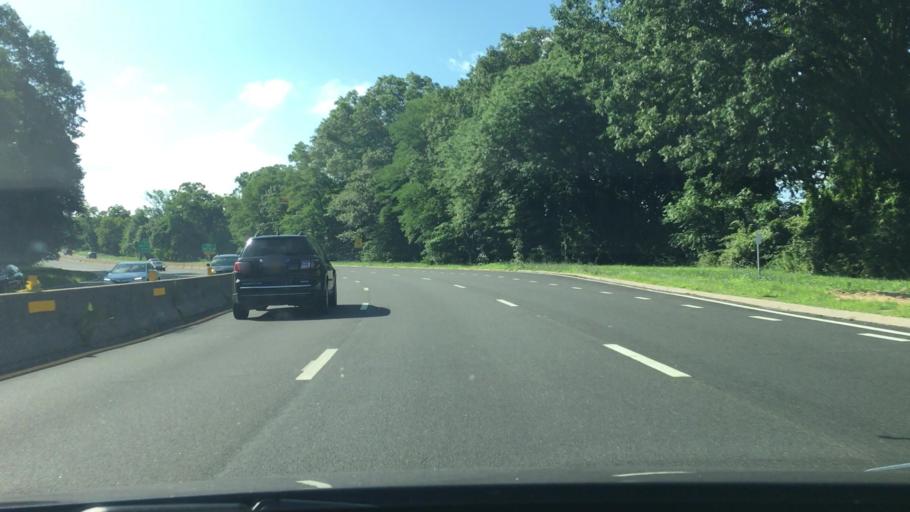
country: US
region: New York
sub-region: Nassau County
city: Bellmore
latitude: 40.6664
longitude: -73.5157
